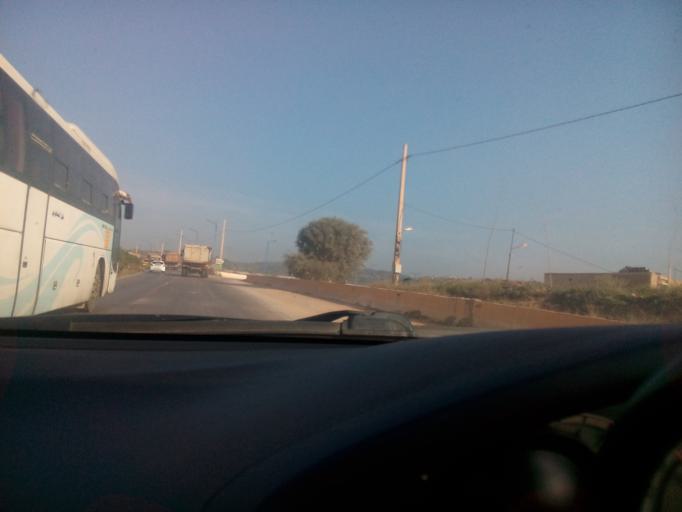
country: DZ
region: Oran
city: Es Senia
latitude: 35.6247
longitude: -0.7187
